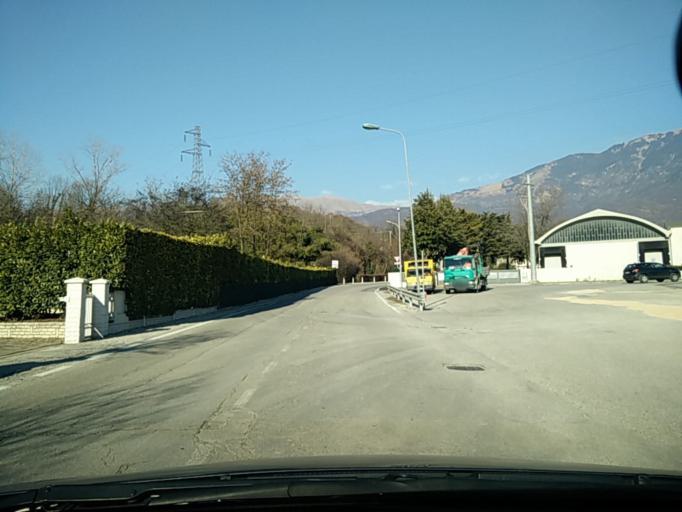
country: IT
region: Veneto
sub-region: Provincia di Treviso
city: Cappella Maggiore
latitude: 45.9859
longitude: 12.3437
